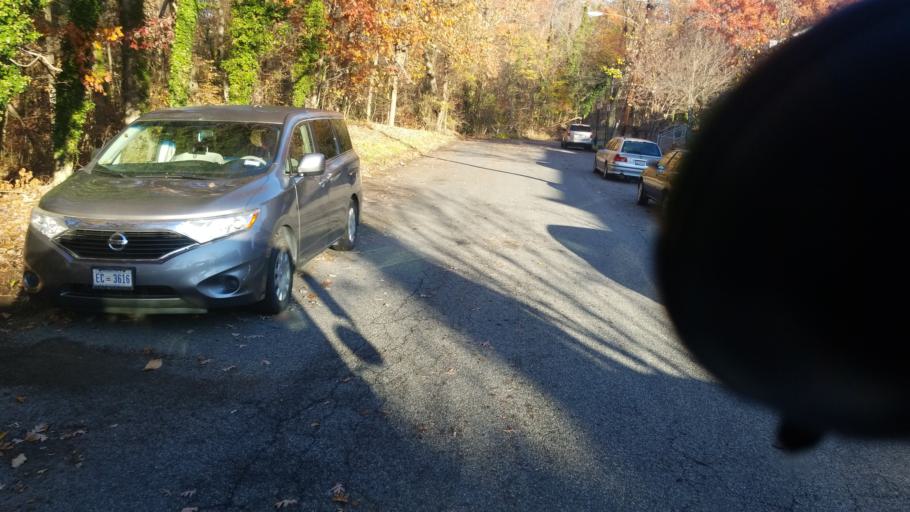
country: US
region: Maryland
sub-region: Prince George's County
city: Coral Hills
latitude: 38.8823
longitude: -76.9438
